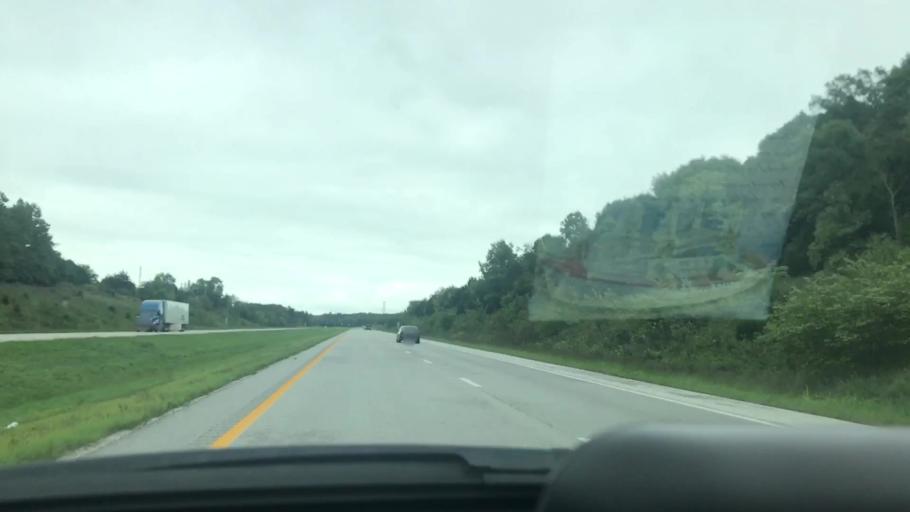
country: US
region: Missouri
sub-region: Greene County
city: Strafford
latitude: 37.3127
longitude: -93.1716
